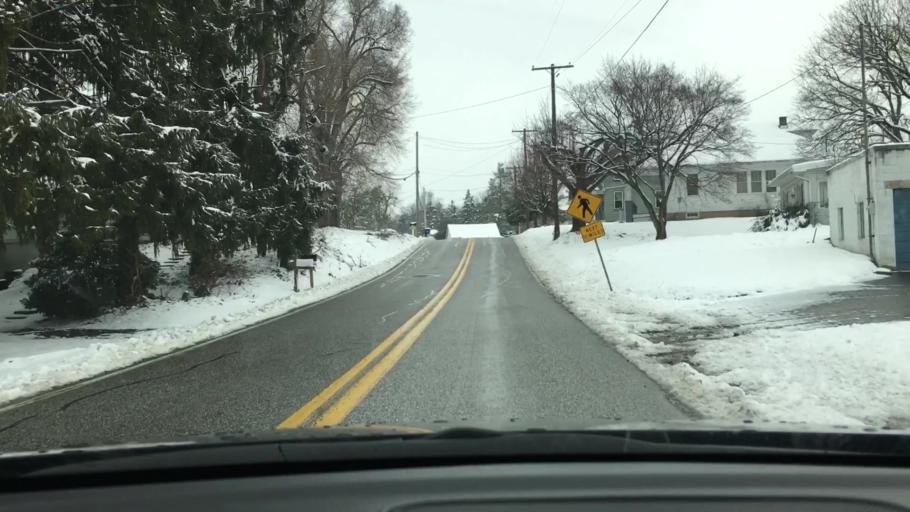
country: US
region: Pennsylvania
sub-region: York County
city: Emigsville
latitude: 40.0058
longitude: -76.7508
